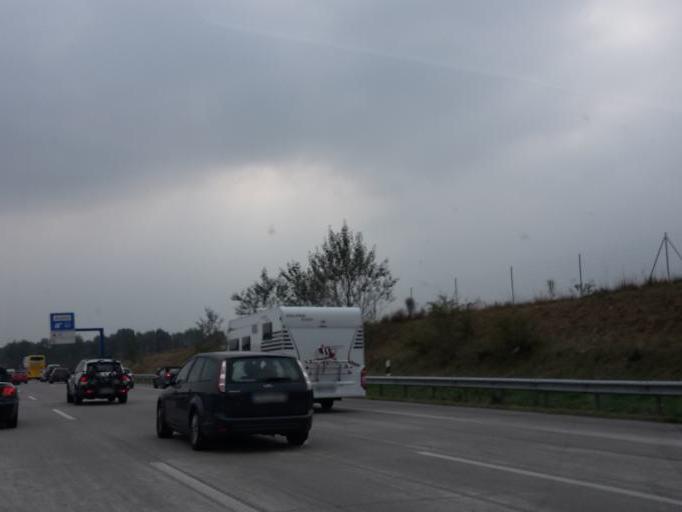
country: DE
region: Lower Saxony
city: Bakum
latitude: 52.7476
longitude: 8.1793
